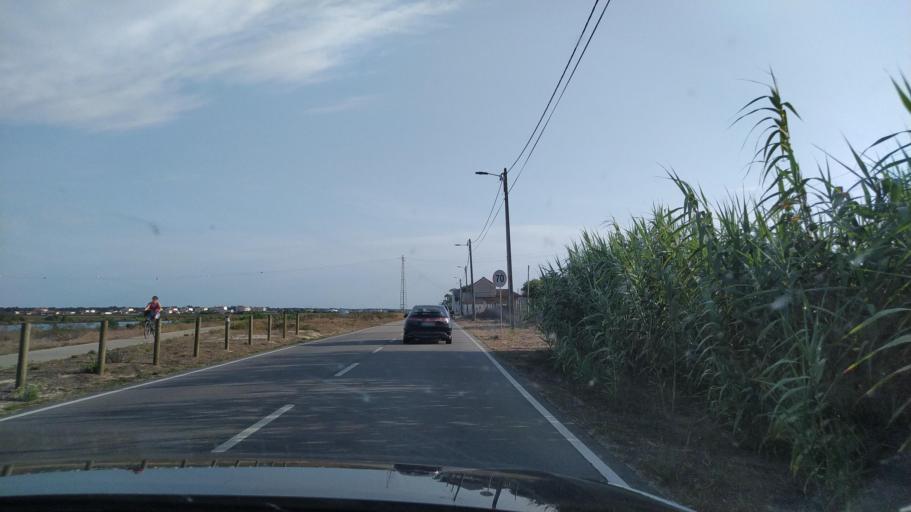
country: PT
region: Aveiro
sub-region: Ilhavo
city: Gafanha da Encarnacao
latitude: 40.5727
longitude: -8.7564
